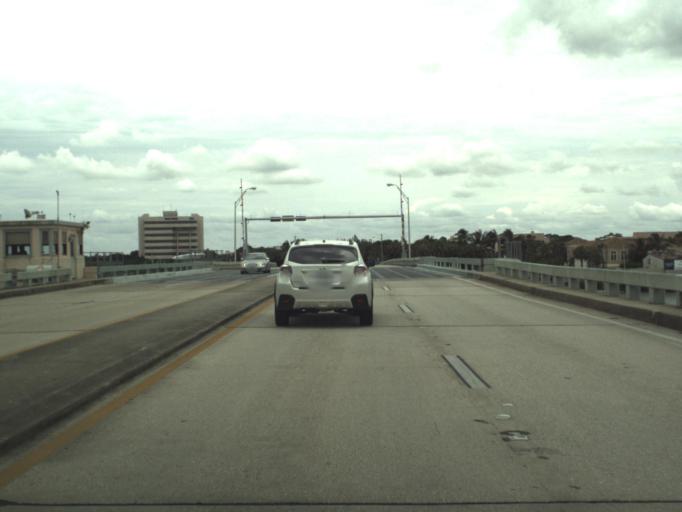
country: US
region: Florida
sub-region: Palm Beach County
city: Jupiter
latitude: 26.9481
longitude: -80.0851
